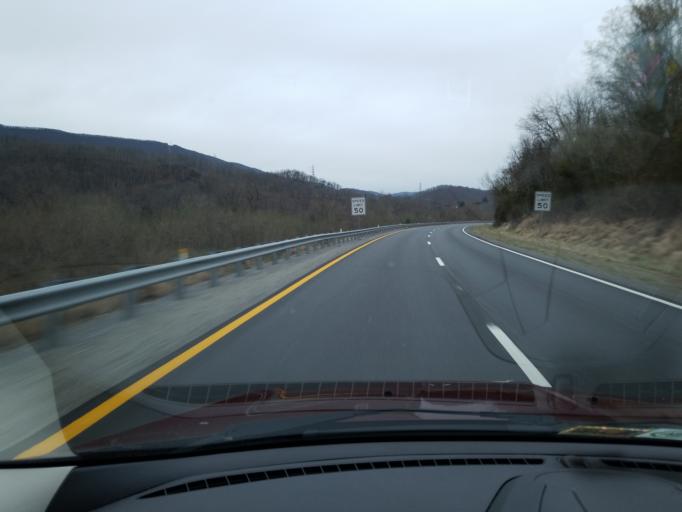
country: US
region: Virginia
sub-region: Giles County
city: Narrows
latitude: 37.3747
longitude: -80.8508
